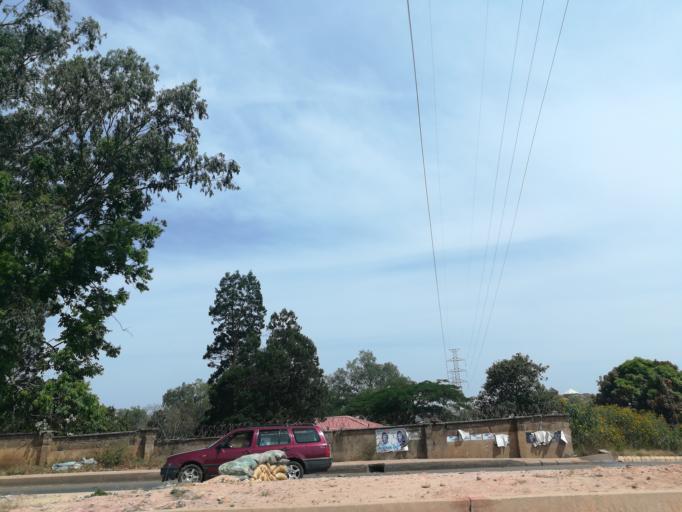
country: NG
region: Plateau
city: Bukuru
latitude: 9.8386
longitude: 8.8659
